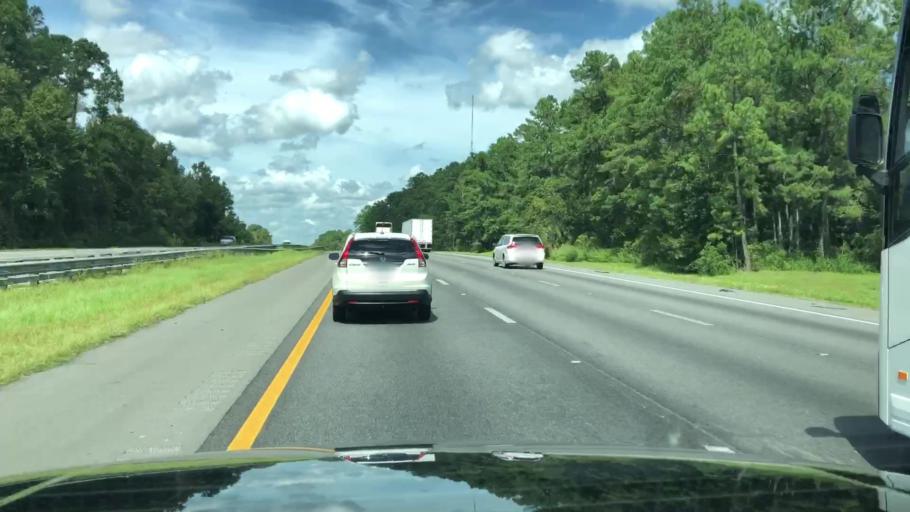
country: US
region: Florida
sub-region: Alachua County
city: Gainesville
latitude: 29.5309
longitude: -82.3166
